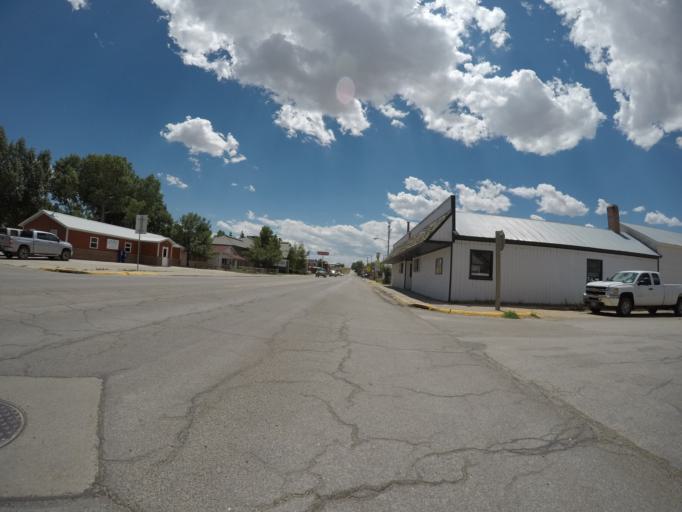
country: US
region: Wyoming
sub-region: Carbon County
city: Saratoga
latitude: 41.4540
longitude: -106.8077
